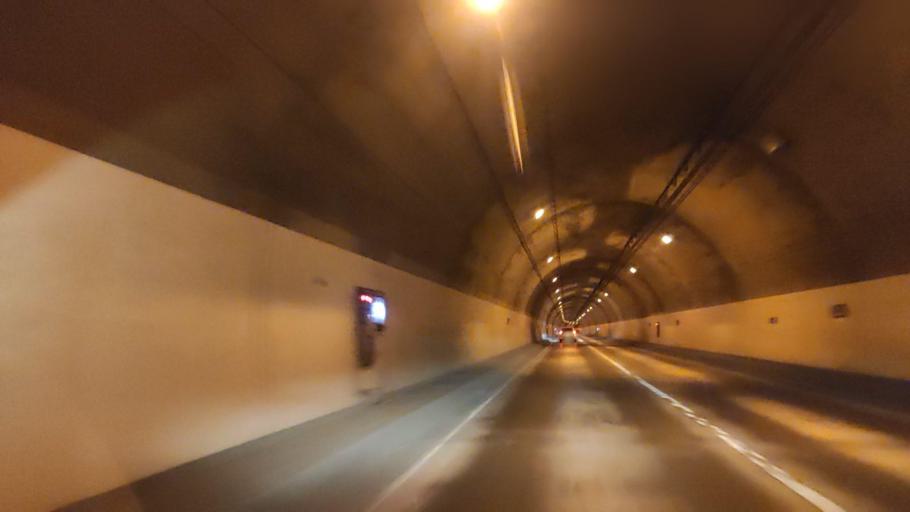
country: JP
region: Hokkaido
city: Ishikari
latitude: 43.4584
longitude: 141.4067
